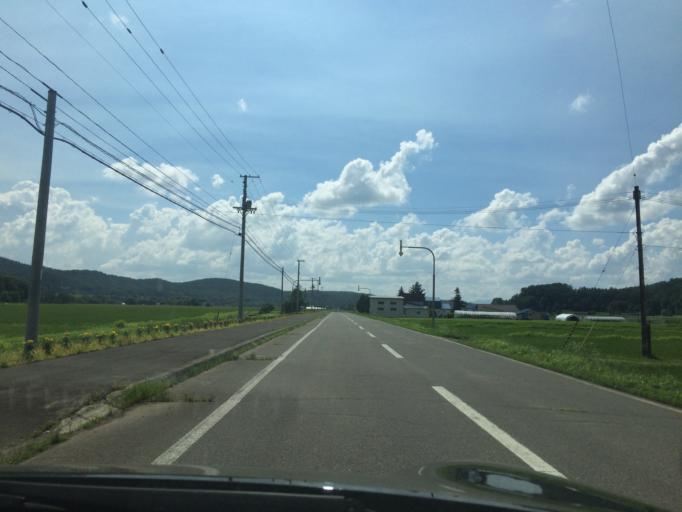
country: JP
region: Hokkaido
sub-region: Asahikawa-shi
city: Asahikawa
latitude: 43.7565
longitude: 142.5395
